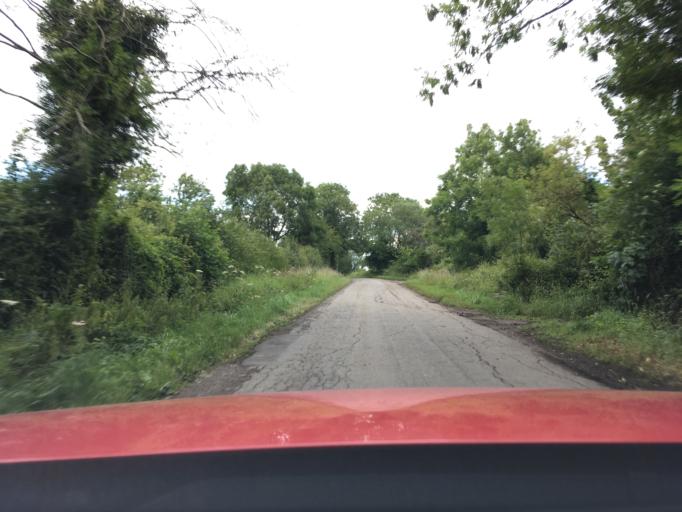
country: GB
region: England
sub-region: Gloucestershire
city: Stonehouse
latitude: 51.7893
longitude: -2.3741
